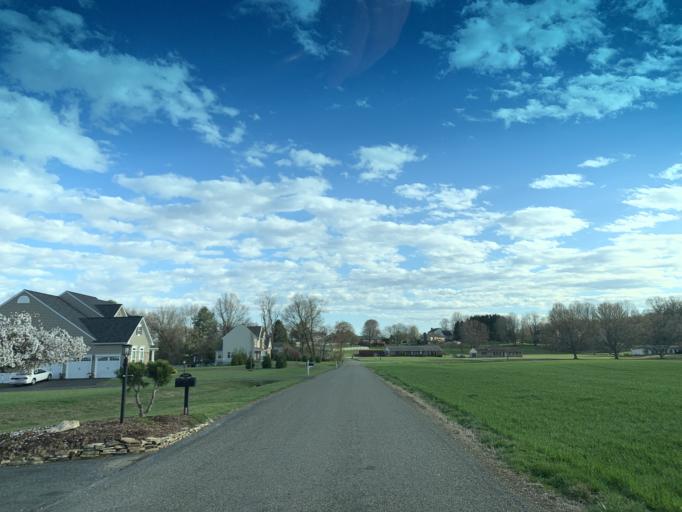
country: US
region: Maryland
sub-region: Harford County
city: South Bel Air
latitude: 39.5706
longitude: -76.2770
